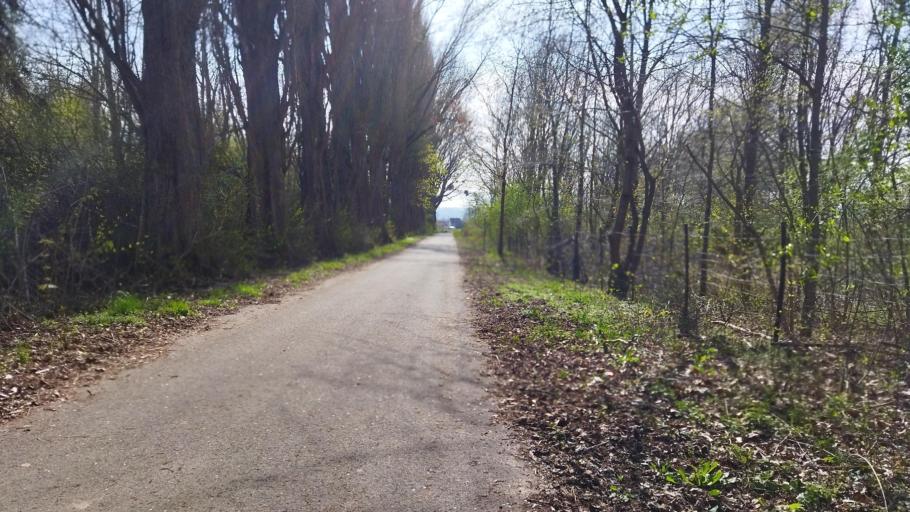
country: DE
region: Lower Saxony
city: Hessisch Oldendorf
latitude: 52.1476
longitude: 9.2768
